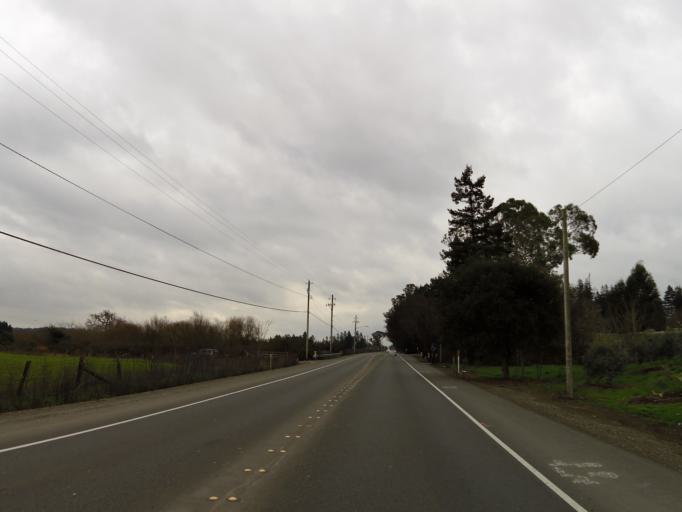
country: US
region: California
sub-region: Sonoma County
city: Rohnert Park
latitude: 38.3431
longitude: -122.6669
